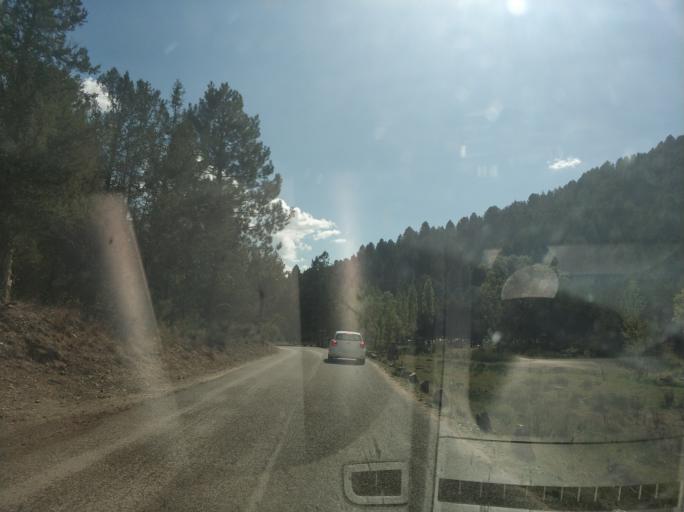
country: ES
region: Castille and Leon
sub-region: Provincia de Soria
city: Ucero
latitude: 41.7348
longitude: -3.0485
